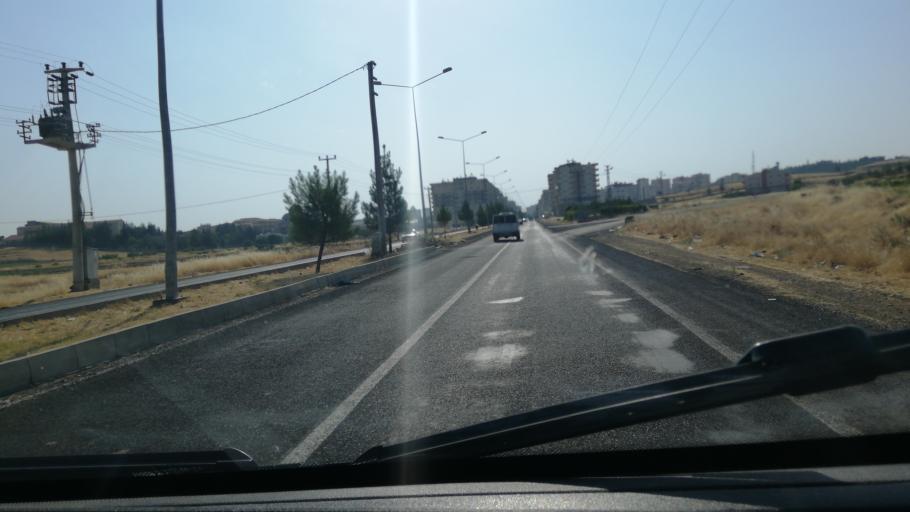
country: TR
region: Mardin
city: Midyat
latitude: 37.4359
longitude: 41.3206
